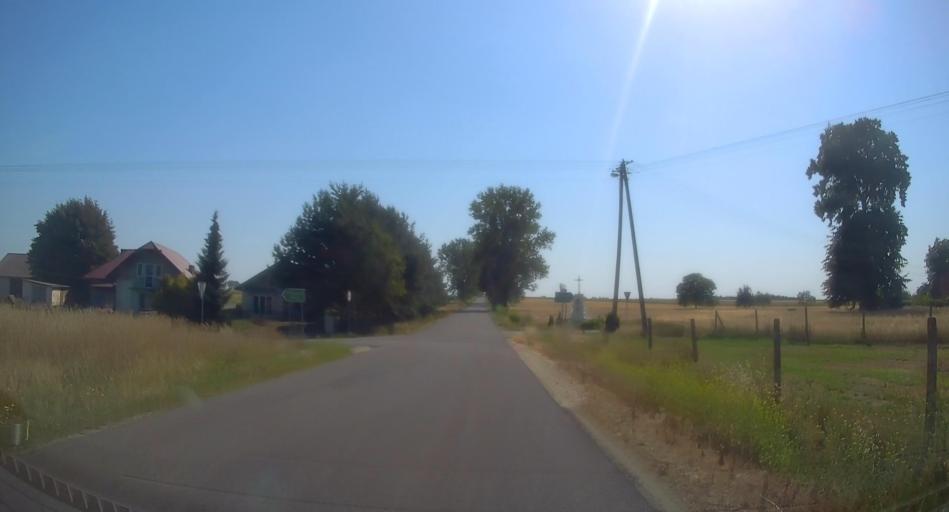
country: PL
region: Lodz Voivodeship
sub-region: Powiat skierniewicki
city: Kaweczyn Nowy
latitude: 51.8763
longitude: 20.2119
